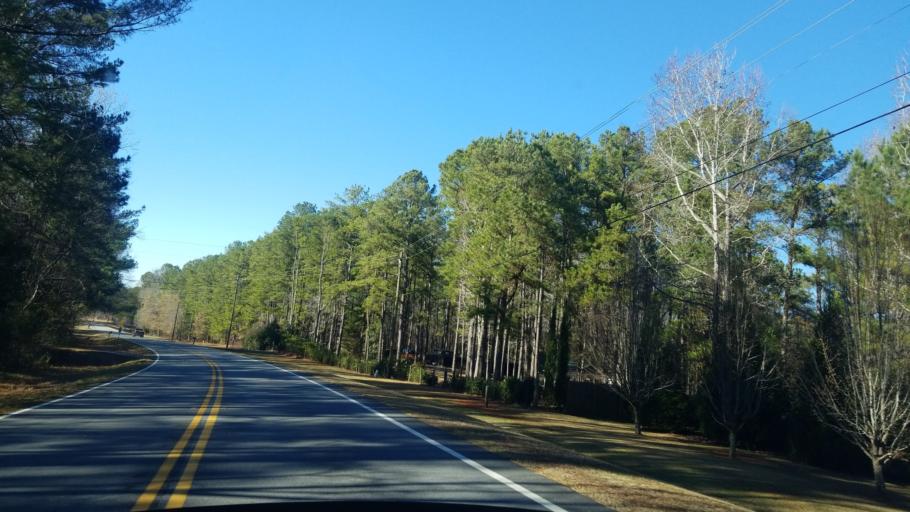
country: US
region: Georgia
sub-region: Harris County
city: Hamilton
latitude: 32.6740
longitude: -84.9079
